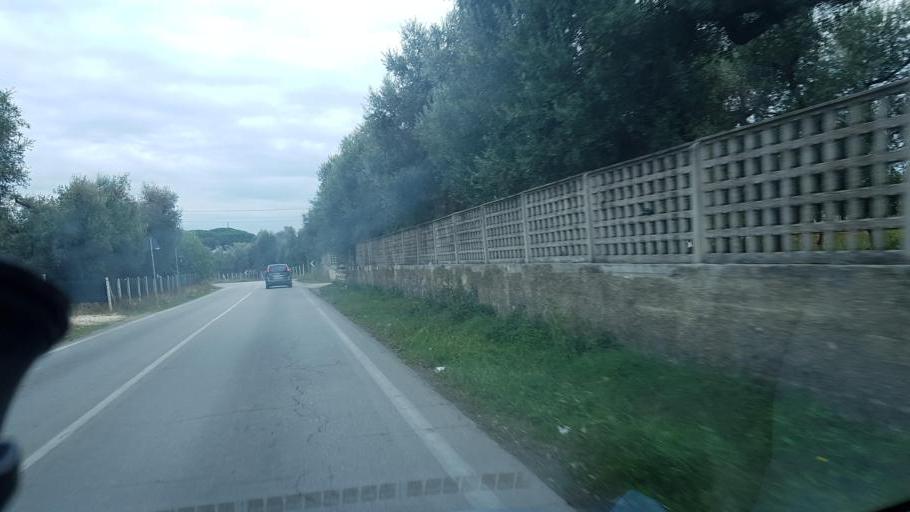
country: IT
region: Apulia
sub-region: Provincia di Brindisi
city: Francavilla Fontana
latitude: 40.5188
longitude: 17.6059
